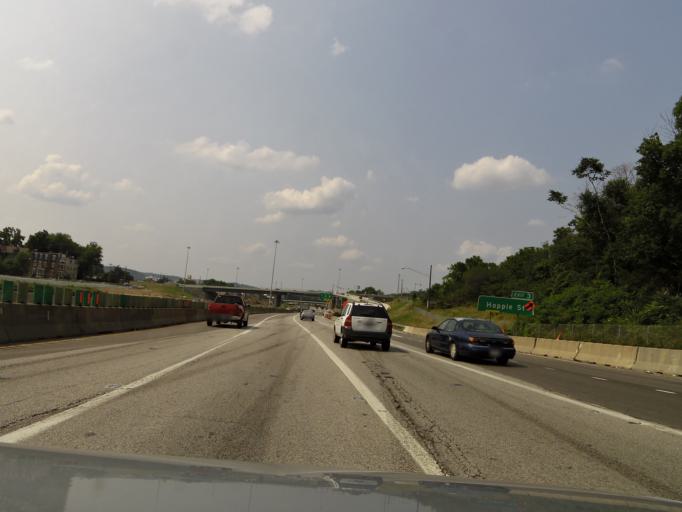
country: US
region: Kentucky
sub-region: Kenton County
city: Ludlow
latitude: 39.1351
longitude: -84.5327
